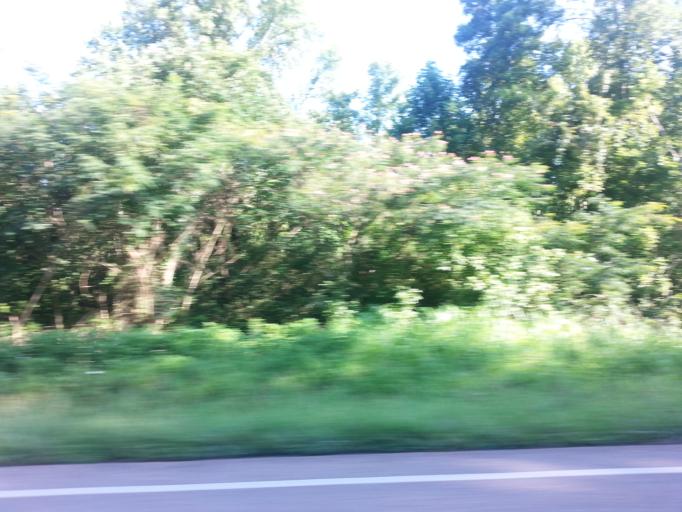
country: US
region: Tennessee
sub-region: Blount County
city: Louisville
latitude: 35.7946
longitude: -84.0937
